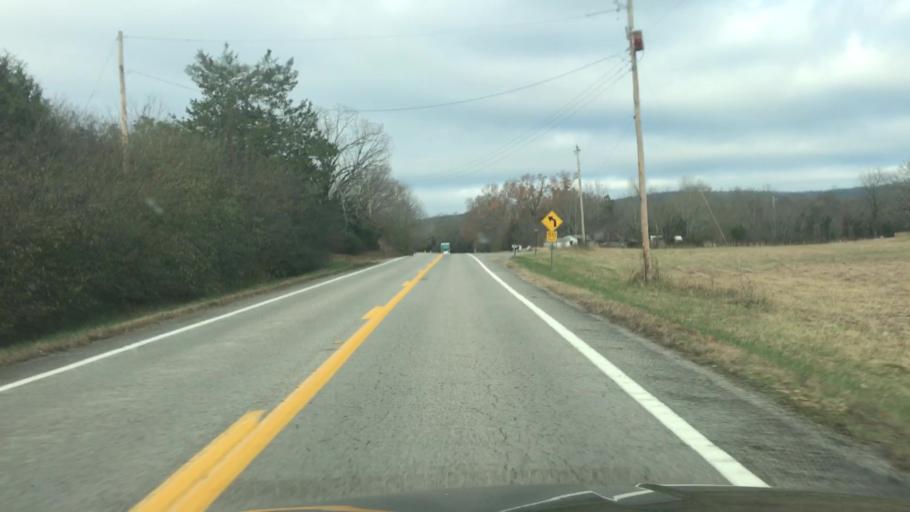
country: US
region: Arkansas
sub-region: Montgomery County
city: Mount Ida
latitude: 34.6566
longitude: -93.7599
